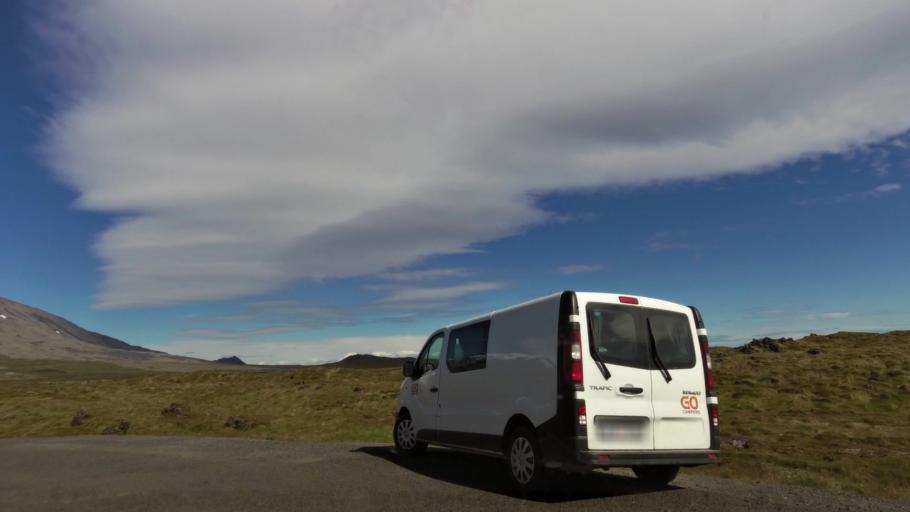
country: IS
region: West
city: Olafsvik
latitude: 64.7534
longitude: -23.8950
